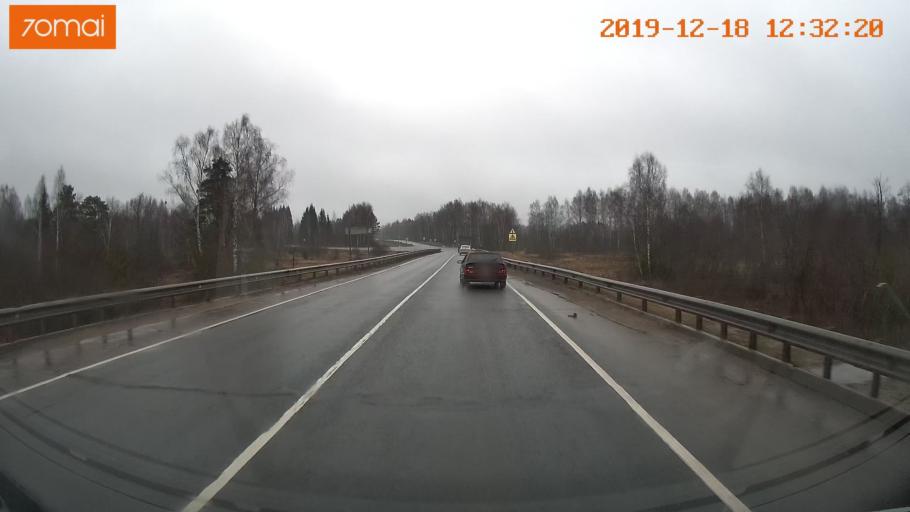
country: RU
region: Moskovskaya
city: Rumyantsevo
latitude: 56.1051
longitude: 36.5497
